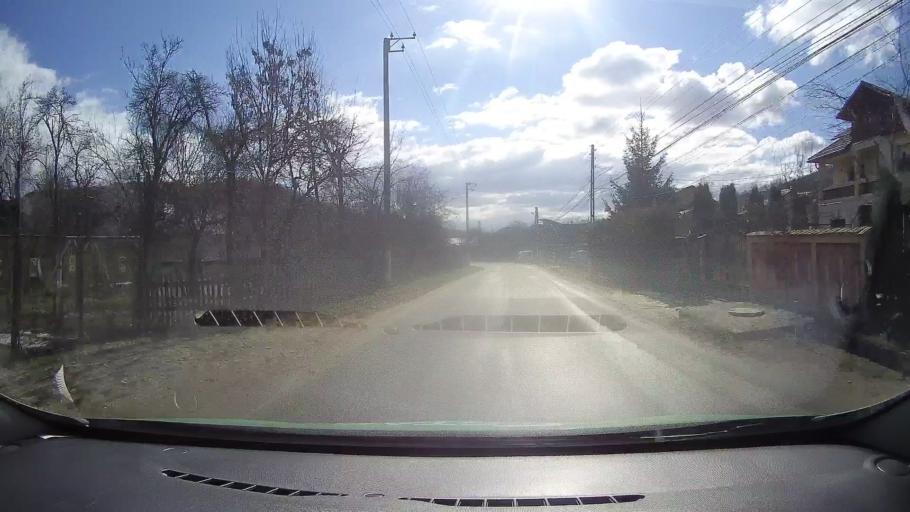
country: RO
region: Dambovita
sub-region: Comuna Runcu
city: Runcu
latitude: 45.1726
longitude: 25.3921
